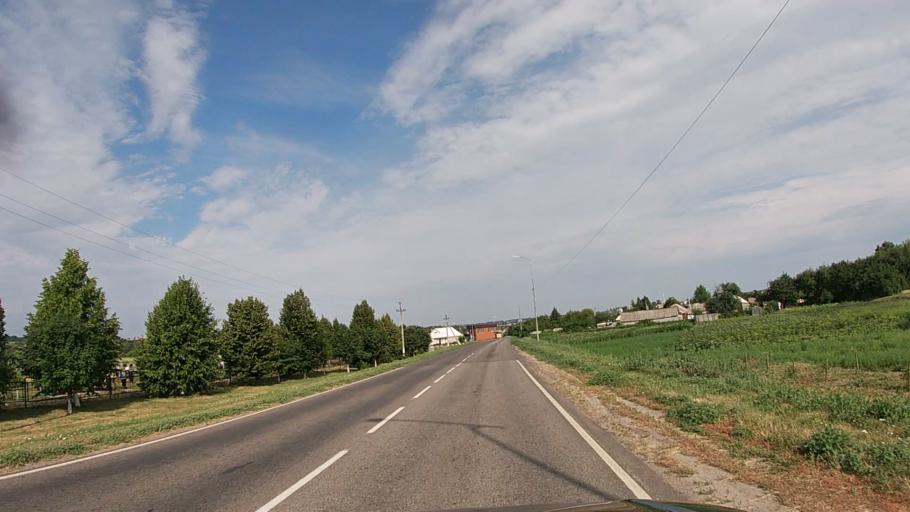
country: RU
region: Belgorod
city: Krasnaya Yaruga
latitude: 50.7989
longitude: 35.6789
